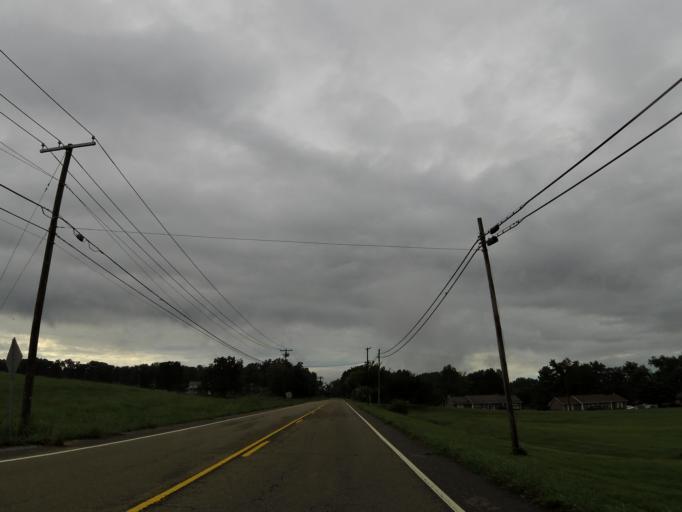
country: US
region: Tennessee
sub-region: Knox County
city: Knoxville
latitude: 35.8788
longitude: -83.9386
